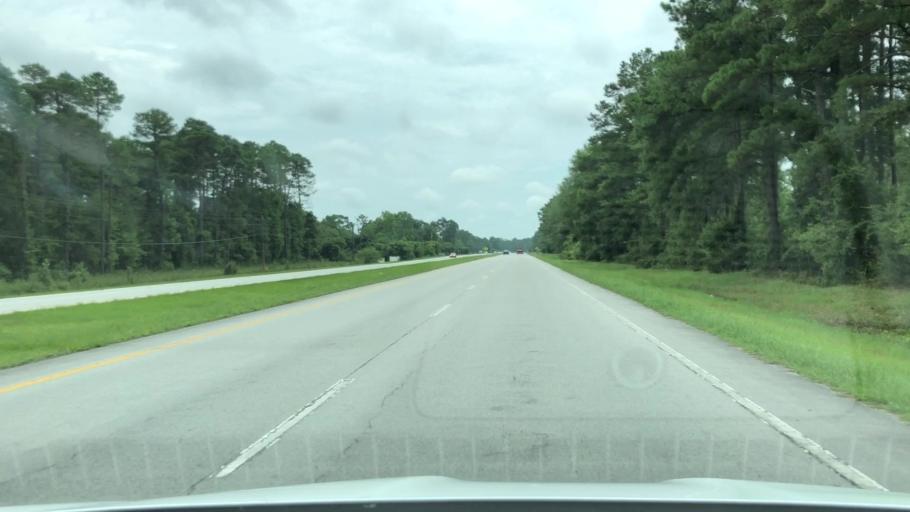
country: US
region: North Carolina
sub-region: Craven County
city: Havelock
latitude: 34.8338
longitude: -76.8807
